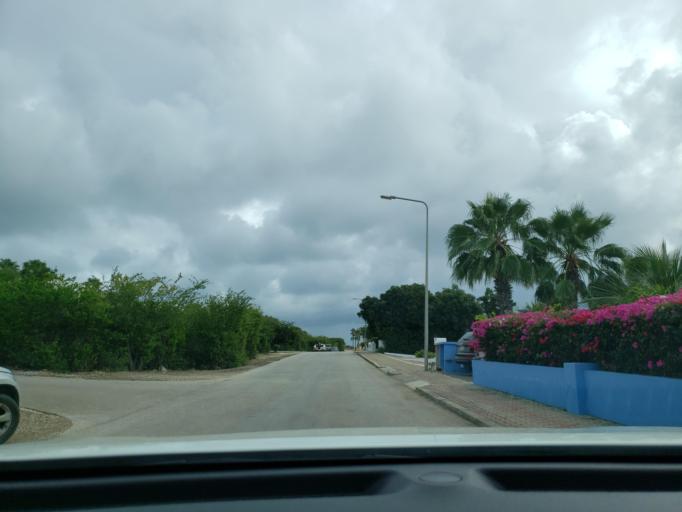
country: CW
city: Dorp Soto
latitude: 12.1995
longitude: -69.0769
